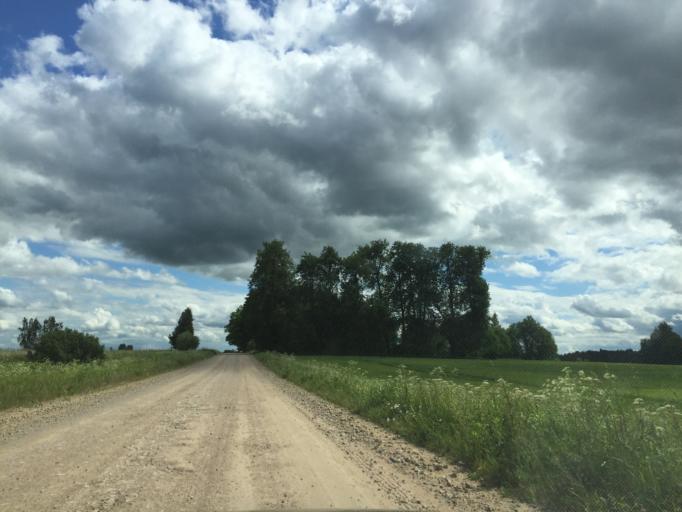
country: LV
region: Vecumnieki
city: Vecumnieki
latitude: 56.4815
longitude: 24.4152
